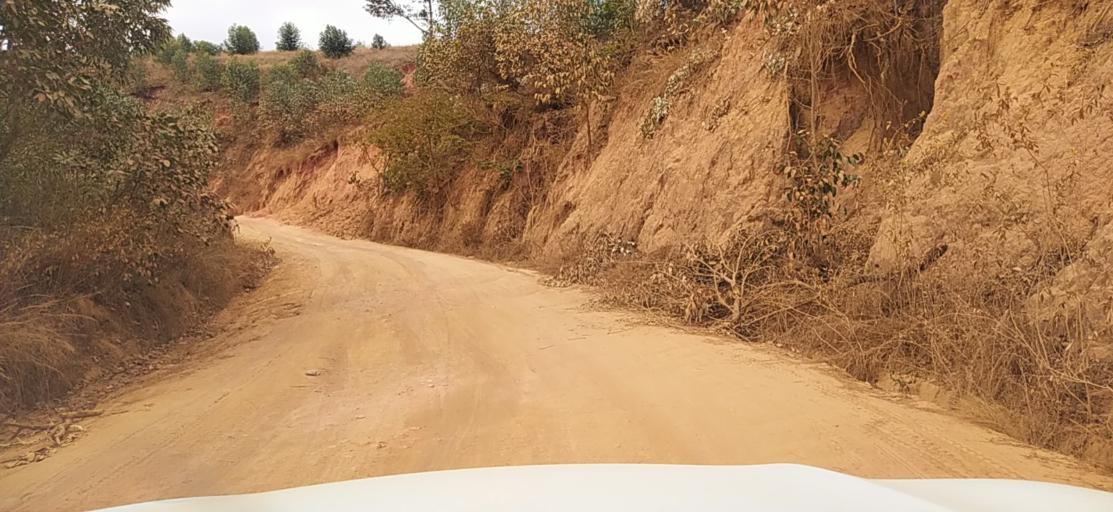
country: MG
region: Alaotra Mangoro
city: Ambatondrazaka
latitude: -17.9990
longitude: 48.2631
